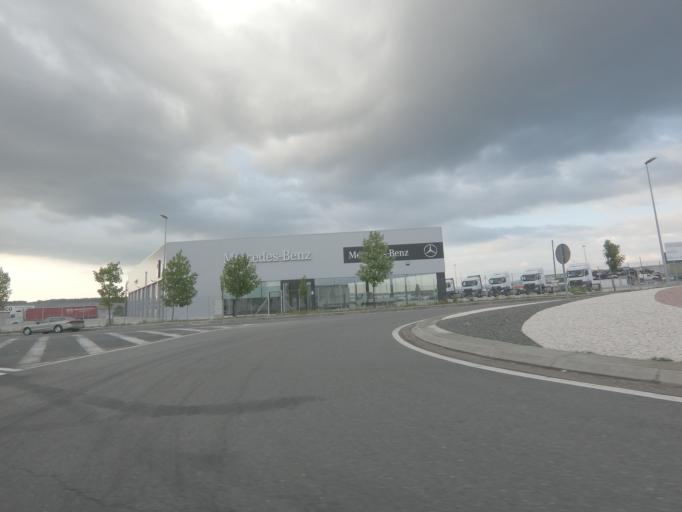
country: ES
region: Galicia
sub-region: Provincia de Ourense
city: Taboadela
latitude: 42.2895
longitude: -7.8142
